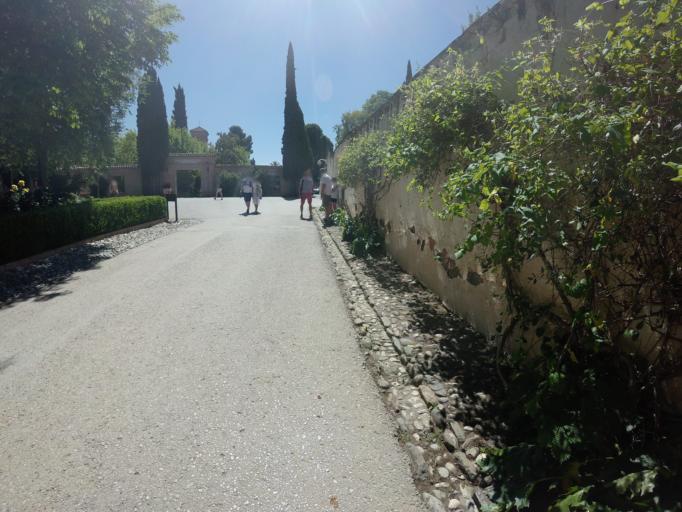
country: ES
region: Andalusia
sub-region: Provincia de Granada
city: Granada
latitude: 37.1759
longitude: -3.5883
